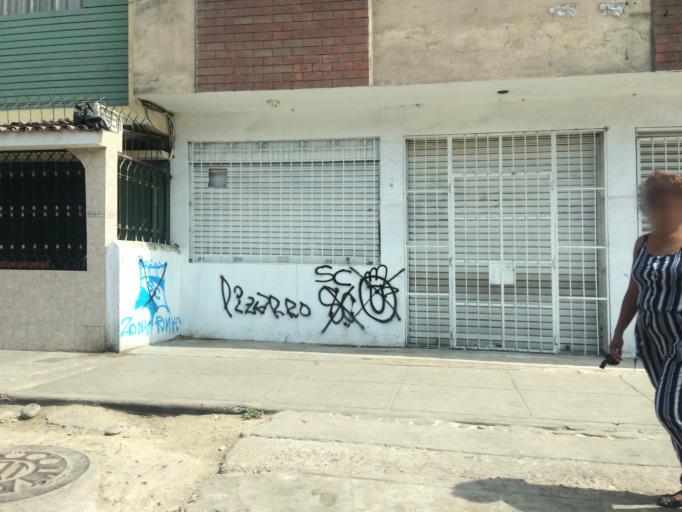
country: PE
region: Lima
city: Lima
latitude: -12.0298
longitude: -77.0363
